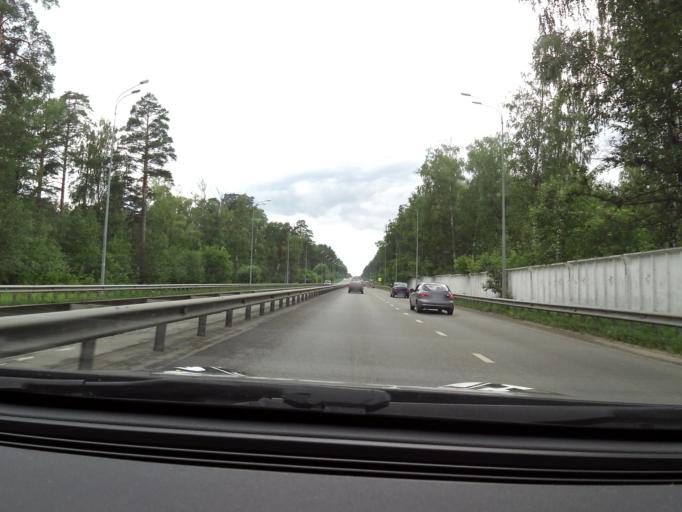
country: RU
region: Tatarstan
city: Staroye Arakchino
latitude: 55.8391
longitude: 48.9588
